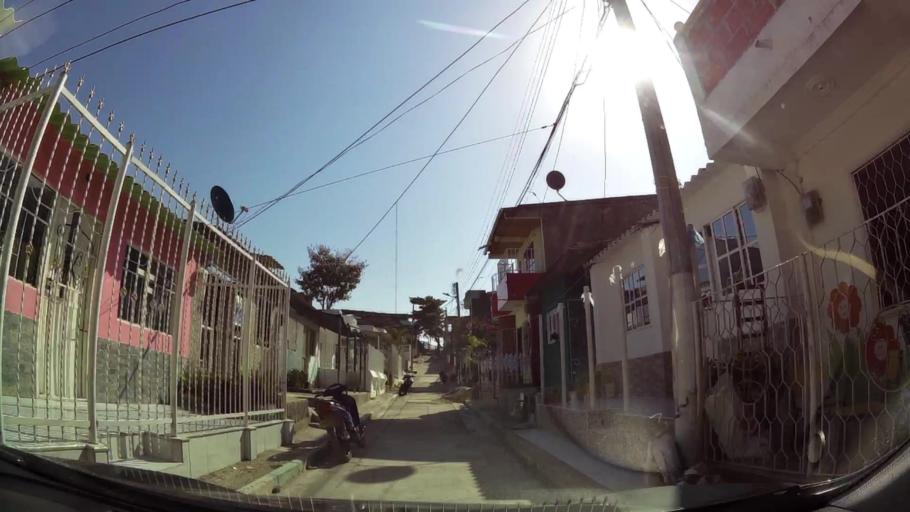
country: CO
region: Bolivar
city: Cartagena
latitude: 10.3708
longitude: -75.5031
